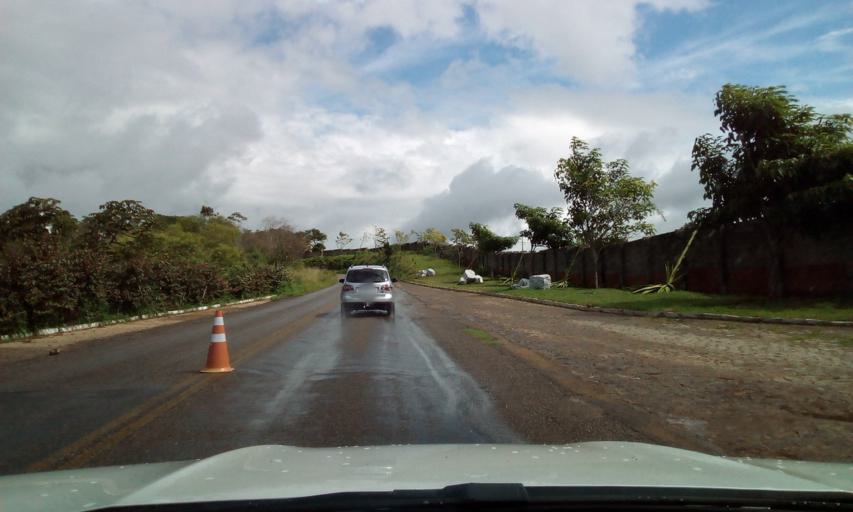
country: BR
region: Paraiba
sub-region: Areia
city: Areia
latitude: -6.9477
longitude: -35.6668
